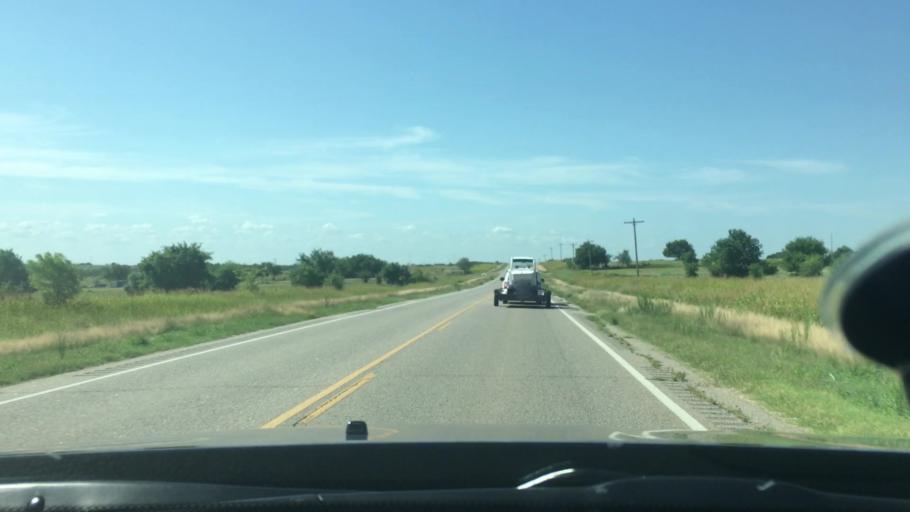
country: US
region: Oklahoma
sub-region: Marshall County
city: Kingston
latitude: 34.0300
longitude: -96.7611
